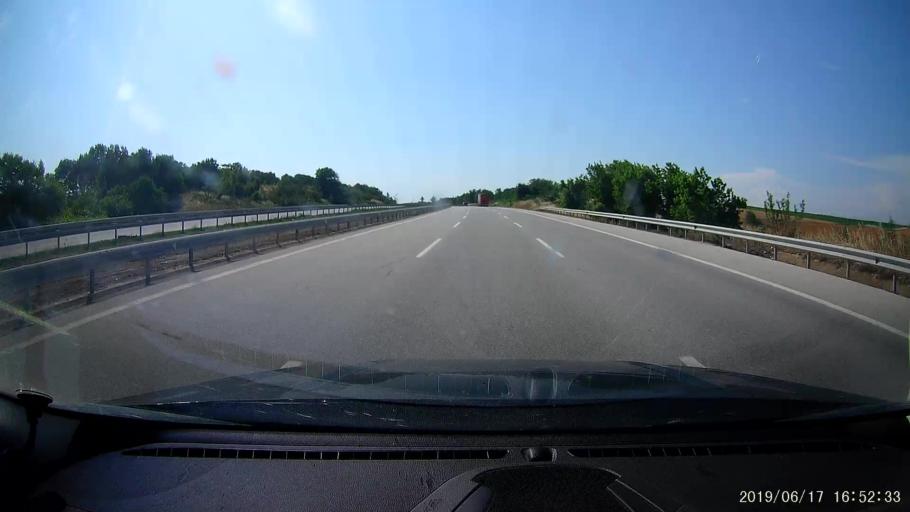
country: TR
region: Kirklareli
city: Inece
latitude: 41.5561
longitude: 27.0492
